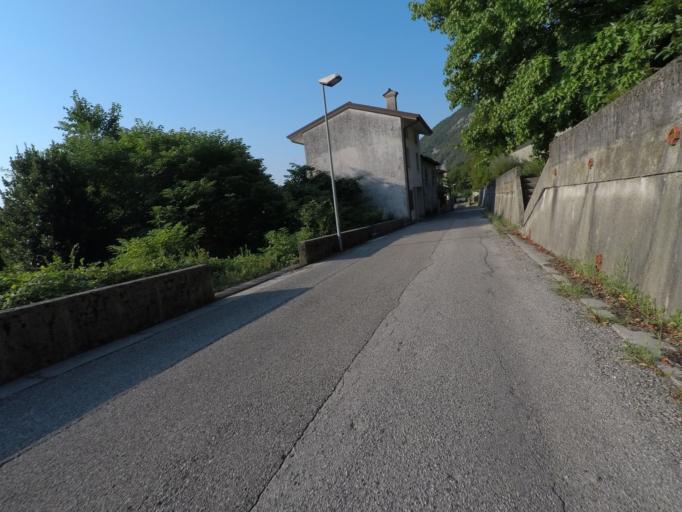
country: IT
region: Friuli Venezia Giulia
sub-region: Provincia di Udine
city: Trasaghis
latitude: 46.2568
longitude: 13.0386
